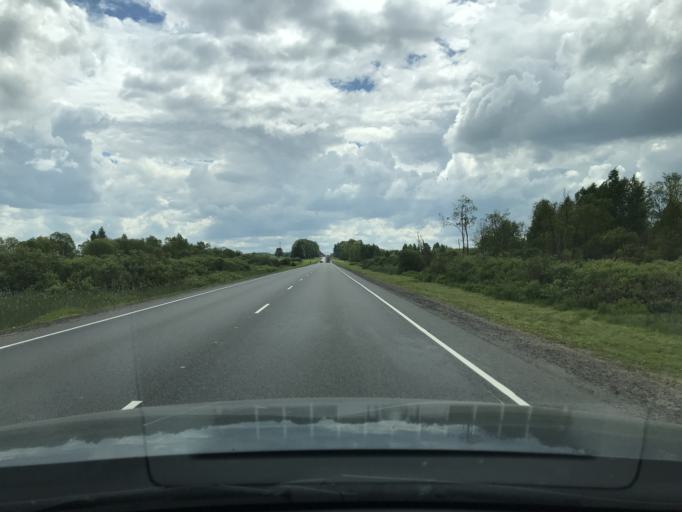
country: RU
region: Kaluga
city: Borovsk
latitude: 55.3643
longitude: 36.4177
